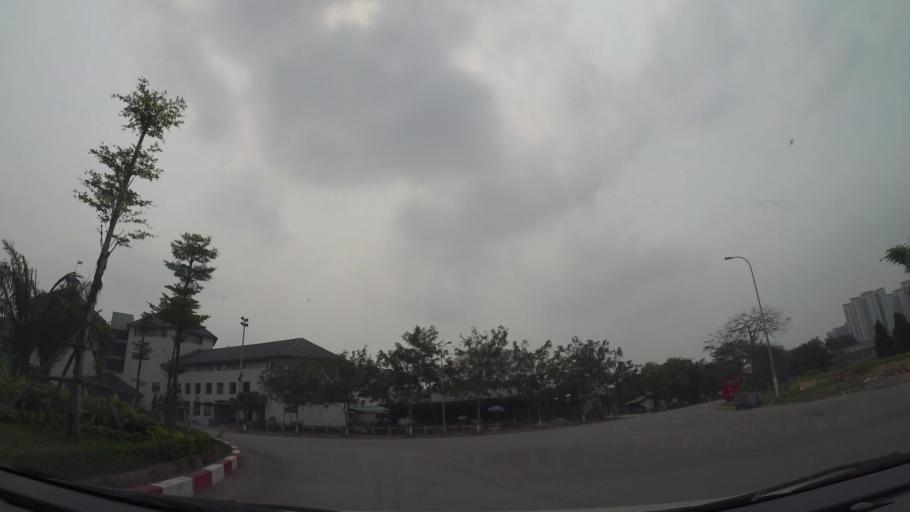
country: VN
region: Ha Noi
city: Cau Dien
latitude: 21.0265
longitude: 105.7591
